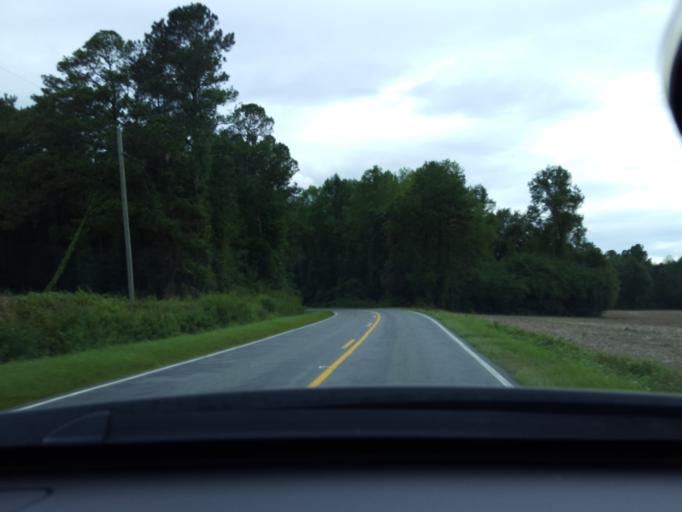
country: US
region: North Carolina
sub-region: Sampson County
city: Roseboro
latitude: 34.7861
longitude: -78.3719
